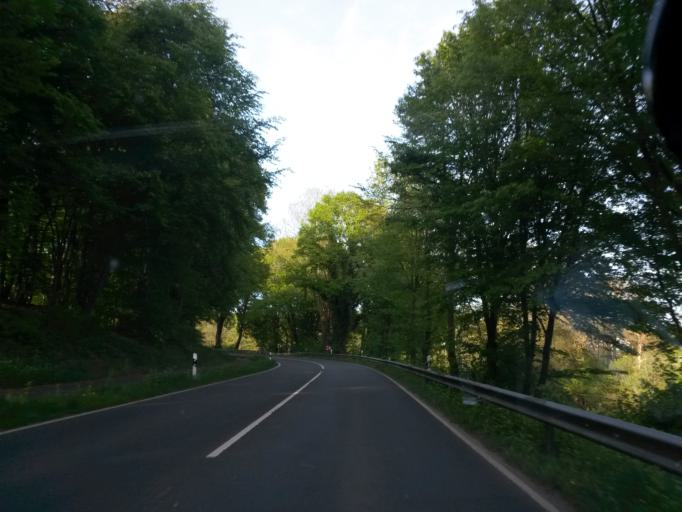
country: DE
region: North Rhine-Westphalia
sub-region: Regierungsbezirk Koln
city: Much
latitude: 50.9310
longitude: 7.4409
